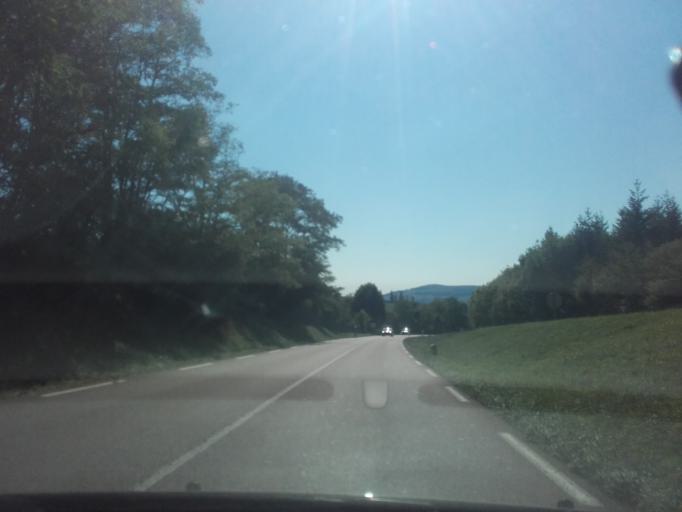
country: FR
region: Bourgogne
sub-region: Departement de la Cote-d'Or
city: Nolay
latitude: 46.9466
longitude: 4.6704
